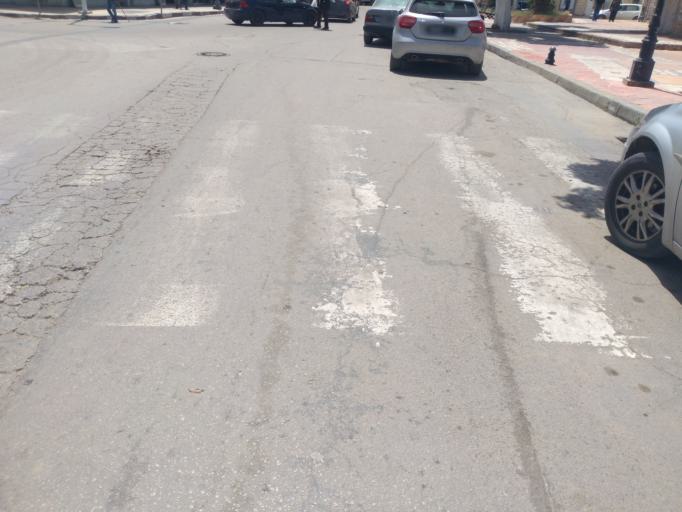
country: TN
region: Al Qayrawan
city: Kairouan
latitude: 35.6732
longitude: 10.1025
